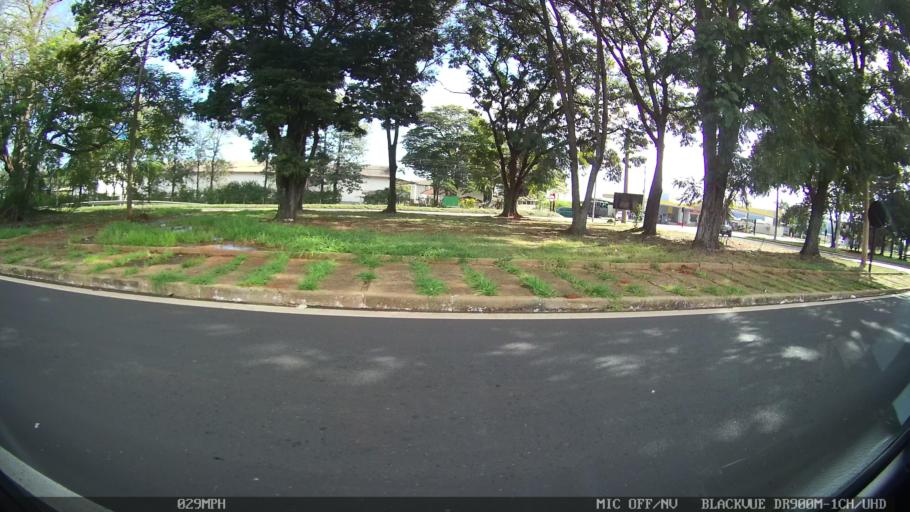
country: BR
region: Sao Paulo
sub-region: Araraquara
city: Araraquara
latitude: -21.8179
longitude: -48.1569
